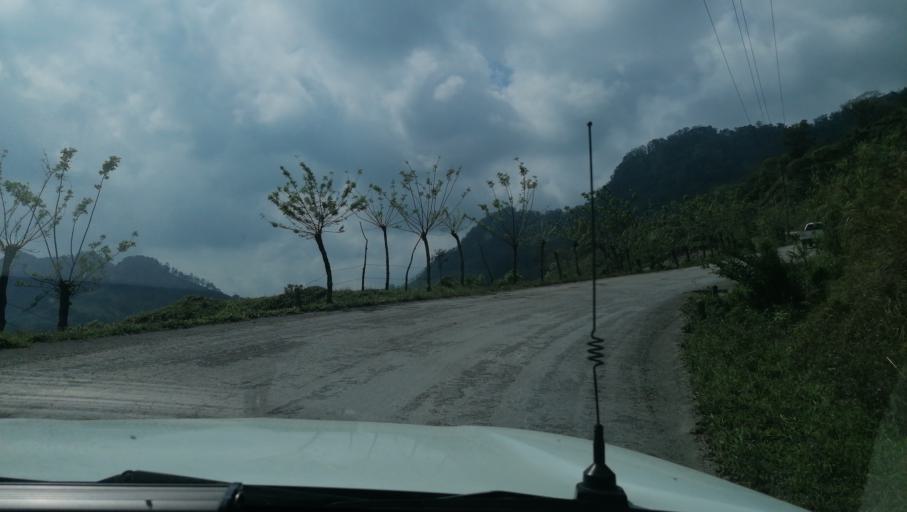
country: MX
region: Chiapas
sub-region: Ocotepec
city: San Pablo Huacano
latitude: 17.2510
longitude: -93.2684
